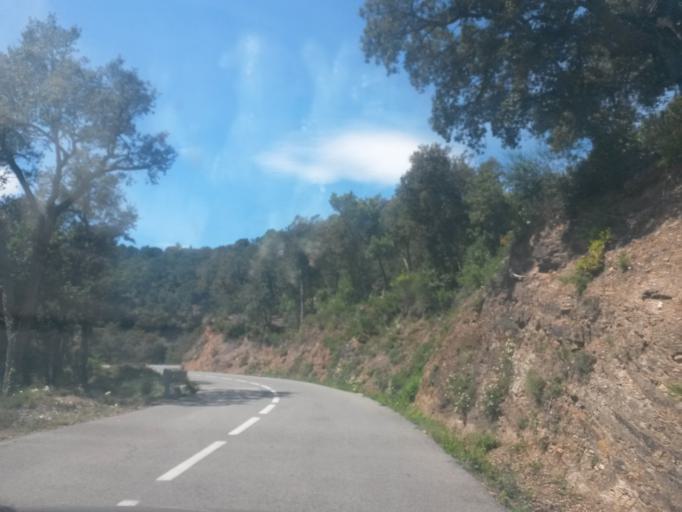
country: ES
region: Catalonia
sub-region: Provincia de Girona
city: Cassa de la Selva
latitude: 41.9274
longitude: 2.9188
